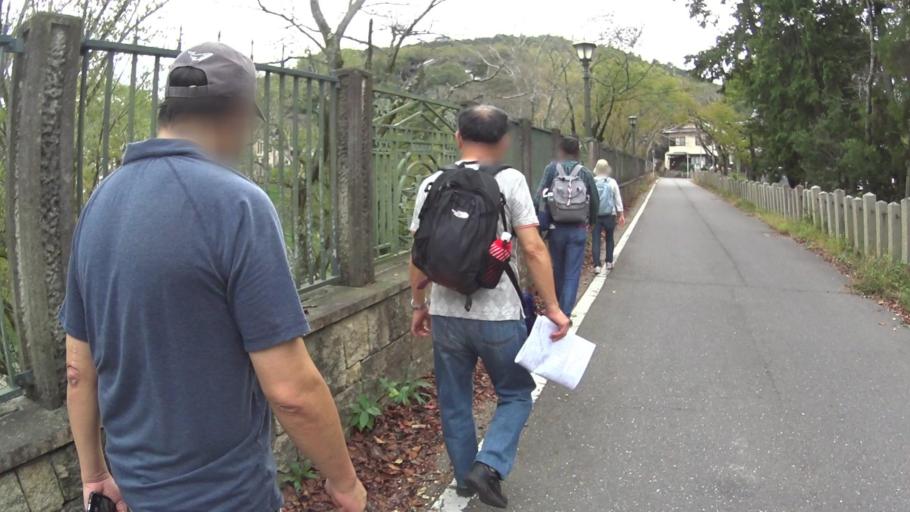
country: JP
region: Osaka
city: Kishiwada
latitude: 34.5115
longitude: 135.3440
